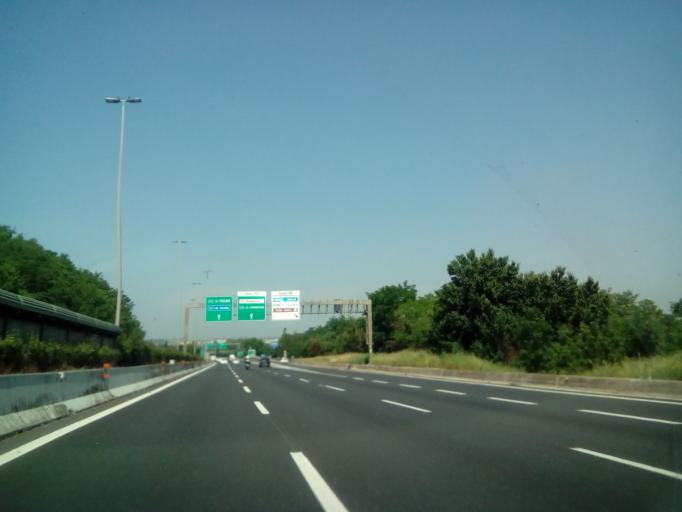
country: IT
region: Latium
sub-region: Citta metropolitana di Roma Capitale
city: Vitinia
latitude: 41.8066
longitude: 12.4245
